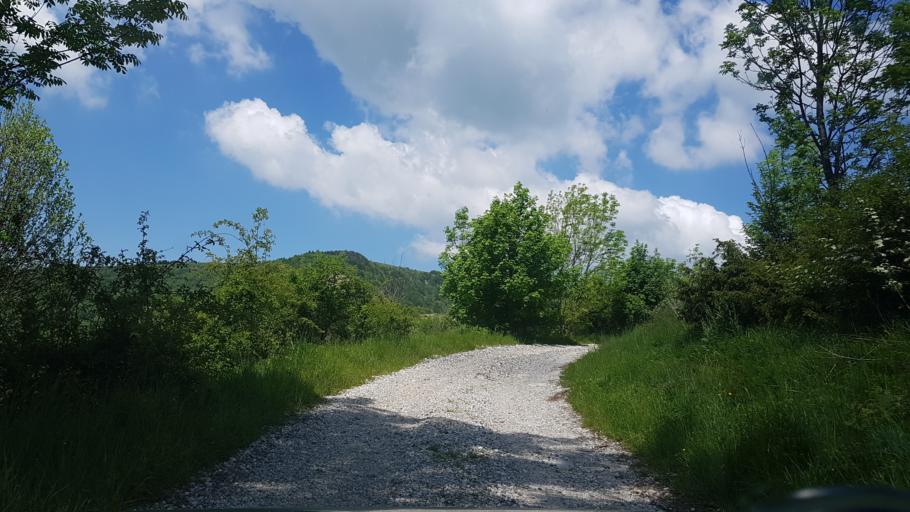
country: IT
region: Friuli Venezia Giulia
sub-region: Provincia di Udine
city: Pulfero
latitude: 46.1799
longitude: 13.4357
